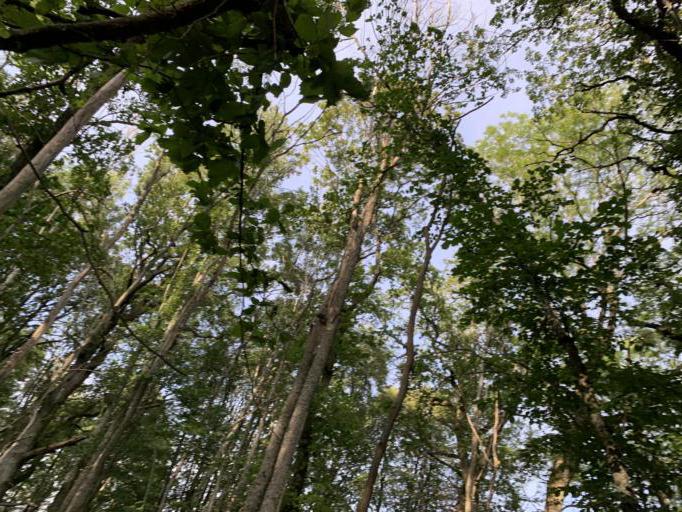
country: SE
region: Vaestmanland
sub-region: Hallstahammars Kommun
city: Kolback
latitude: 59.4709
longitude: 16.2179
